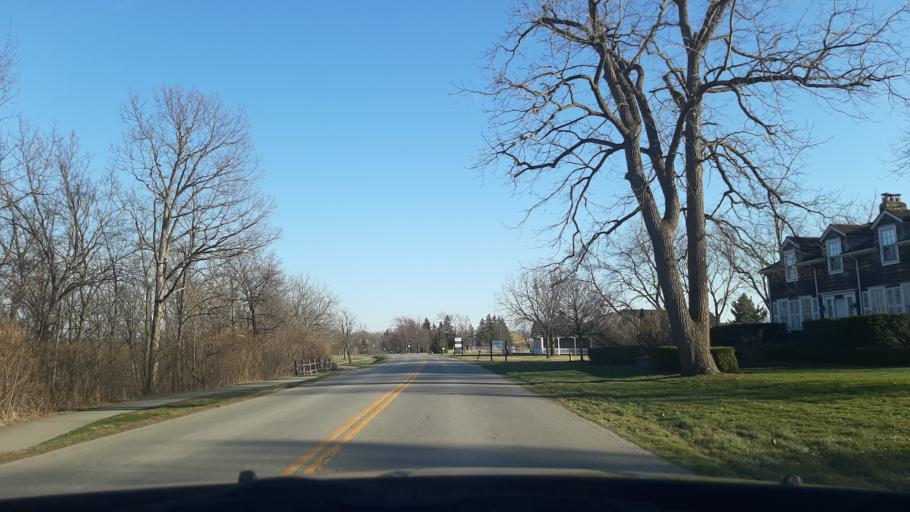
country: US
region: New York
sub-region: Niagara County
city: Youngstown
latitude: 43.2068
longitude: -79.0598
